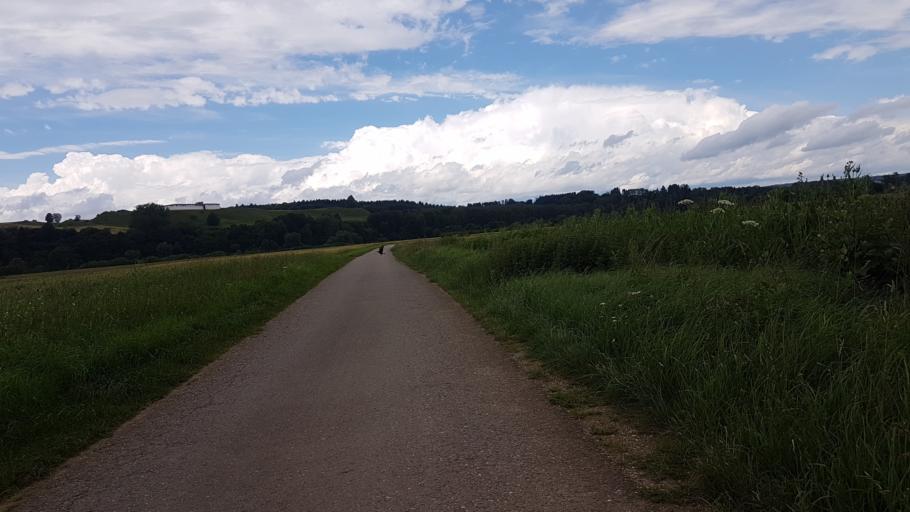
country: DE
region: Baden-Wuerttemberg
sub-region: Tuebingen Region
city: Herbertingen
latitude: 48.0908
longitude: 9.4229
